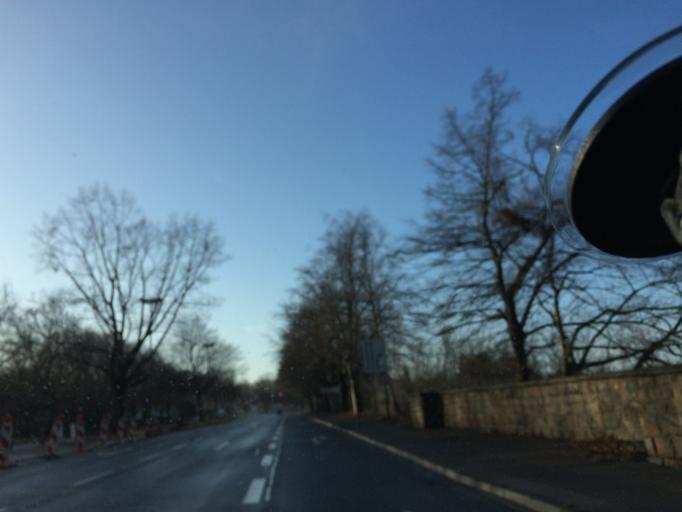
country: DE
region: North Rhine-Westphalia
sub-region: Regierungsbezirk Arnsberg
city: Bochum
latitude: 51.4543
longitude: 7.2254
